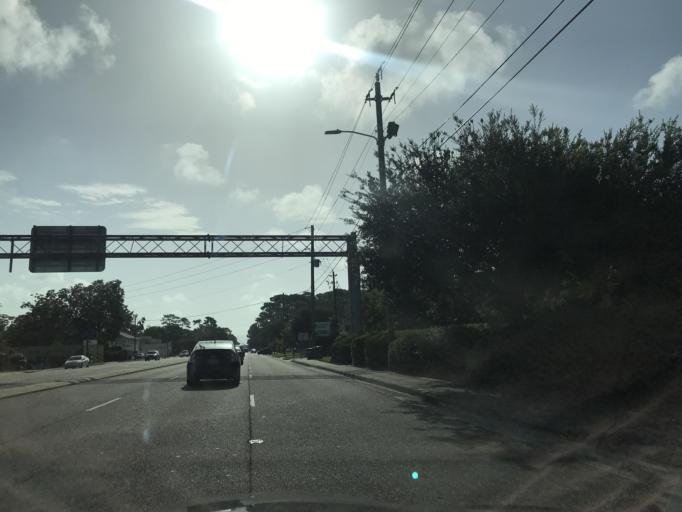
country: US
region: North Carolina
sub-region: New Hanover County
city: Seagate
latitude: 34.2102
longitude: -77.8853
